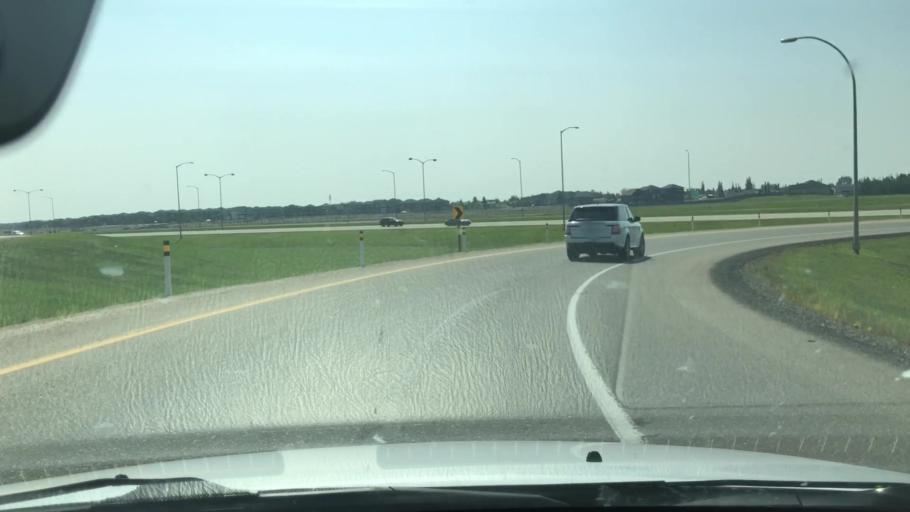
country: CA
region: Alberta
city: Edmonton
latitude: 53.6484
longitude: -113.4889
